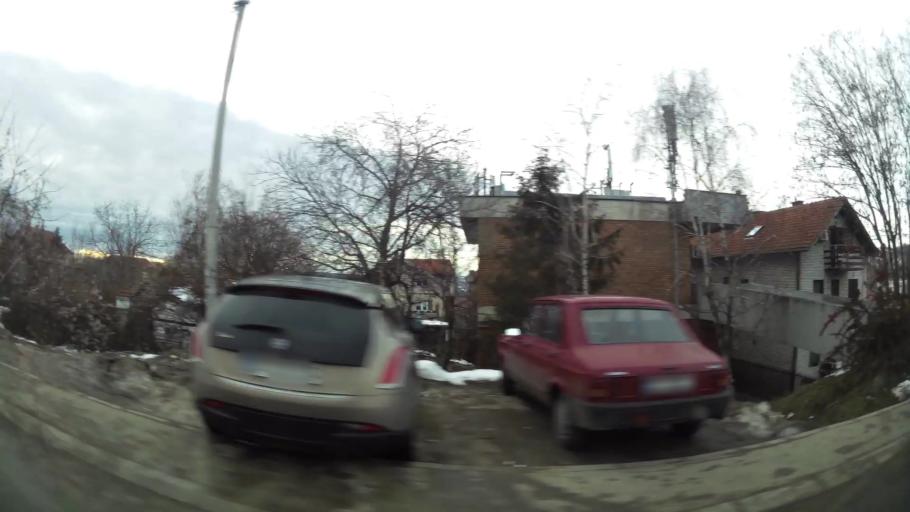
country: RS
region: Central Serbia
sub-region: Belgrade
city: Vozdovac
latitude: 44.7388
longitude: 20.4857
